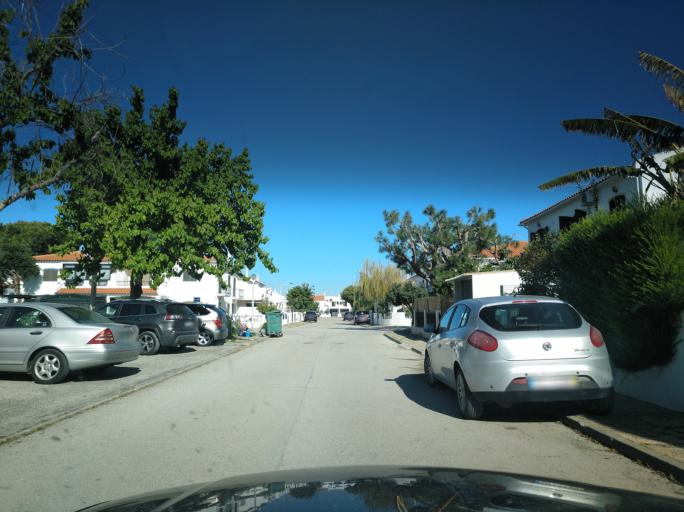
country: PT
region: Faro
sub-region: Vila Real de Santo Antonio
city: Monte Gordo
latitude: 37.1782
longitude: -7.5057
